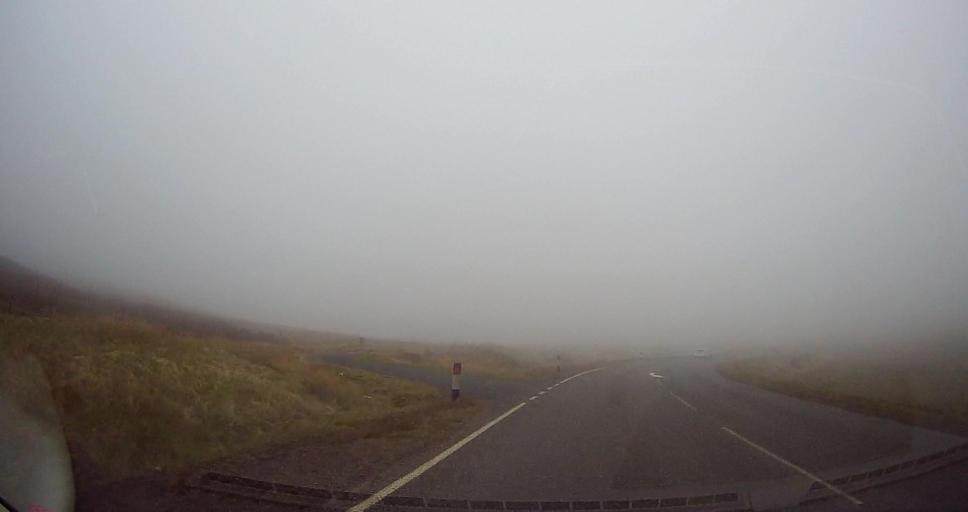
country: GB
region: Scotland
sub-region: Shetland Islands
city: Lerwick
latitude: 60.1384
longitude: -1.2261
